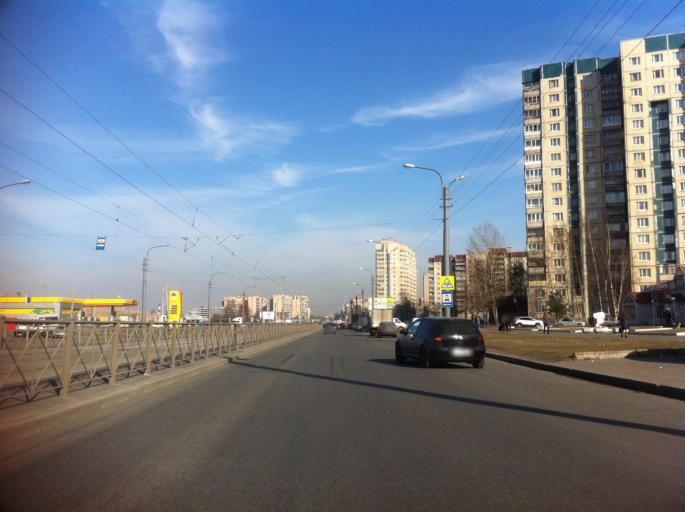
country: RU
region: St.-Petersburg
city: Dachnoye
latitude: 59.8599
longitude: 30.2150
